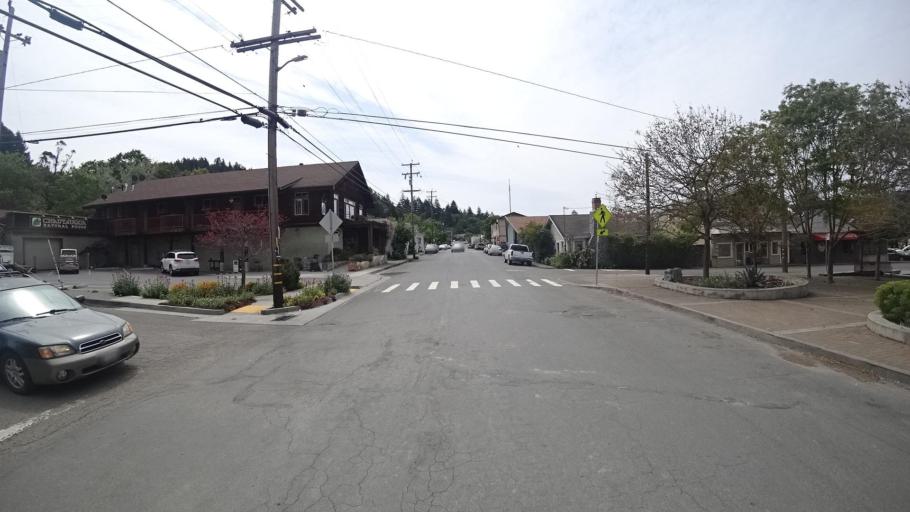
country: US
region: California
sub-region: Humboldt County
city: Redway
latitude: 40.1008
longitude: -123.7937
